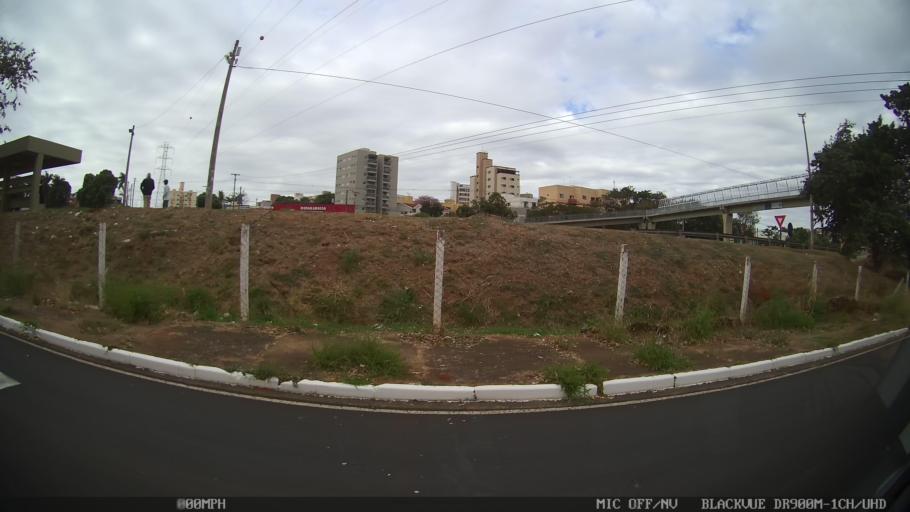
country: BR
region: Sao Paulo
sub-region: Sao Jose Do Rio Preto
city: Sao Jose do Rio Preto
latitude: -20.8236
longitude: -49.3994
